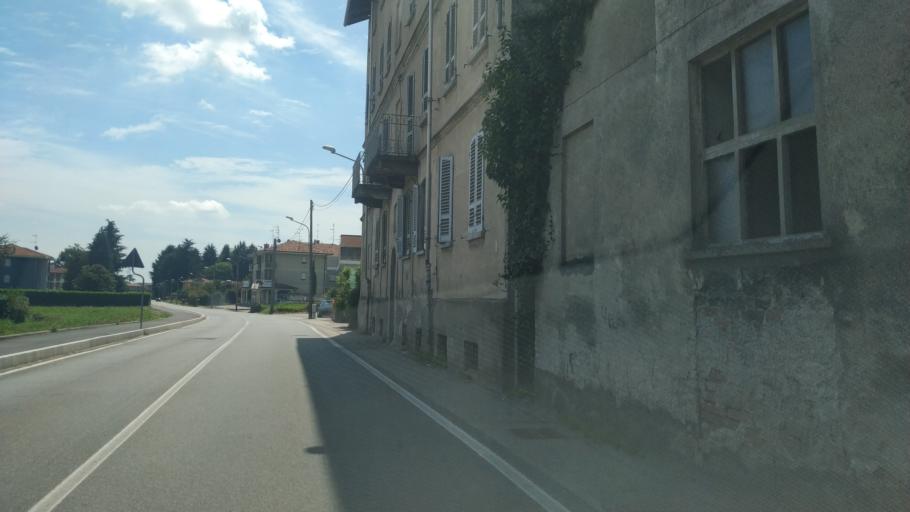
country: IT
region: Piedmont
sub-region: Provincia di Novara
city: Borgomanero
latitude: 45.6993
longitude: 8.4488
